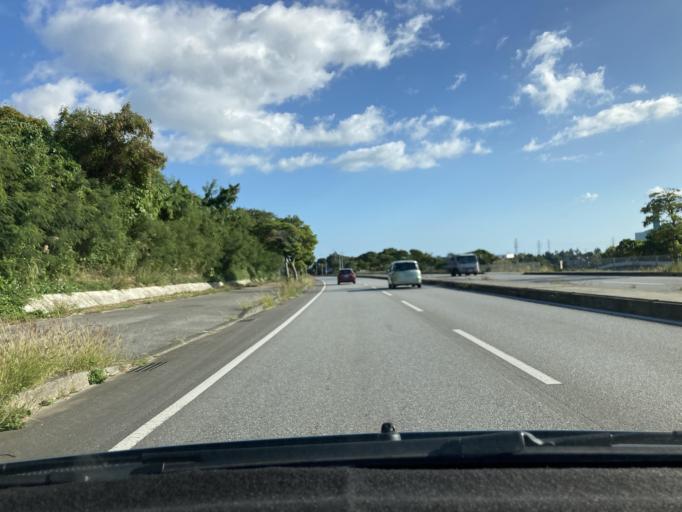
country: JP
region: Okinawa
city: Ishikawa
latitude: 26.4051
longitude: 127.8226
